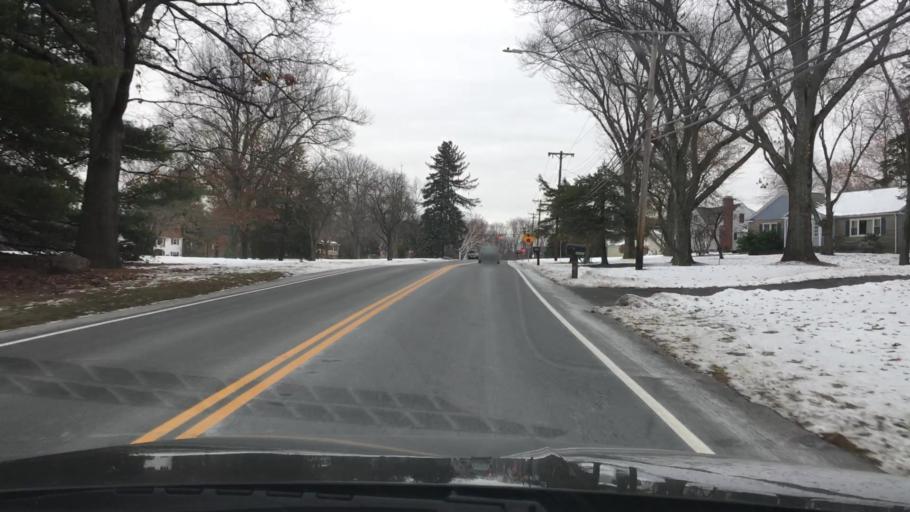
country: US
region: Connecticut
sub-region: Hartford County
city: Manchester
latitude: 41.8347
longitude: -72.5462
